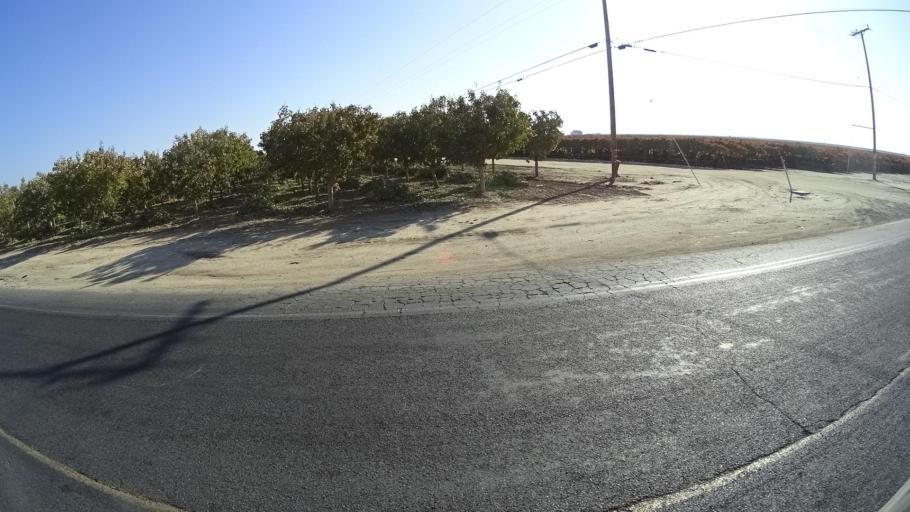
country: US
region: California
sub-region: Tulare County
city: Richgrove
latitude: 35.7473
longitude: -119.1416
